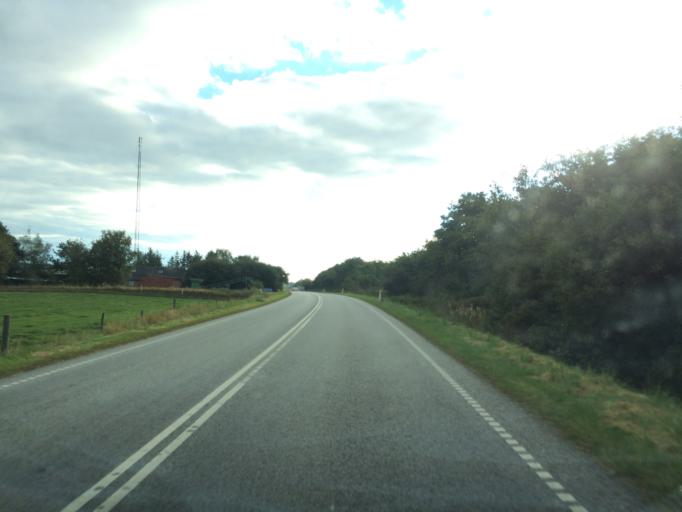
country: DK
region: Central Jutland
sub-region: Herning Kommune
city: Kibaek
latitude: 55.9453
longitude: 8.7718
